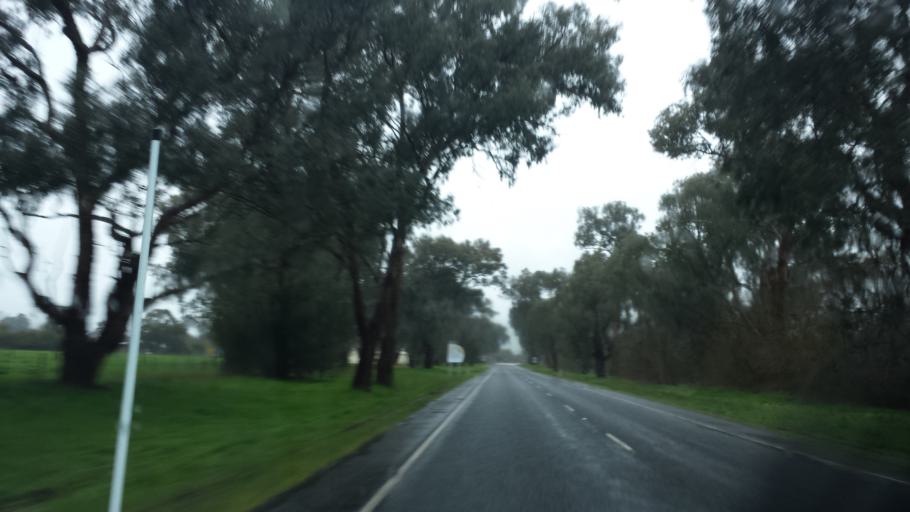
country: AU
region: Victoria
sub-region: Wangaratta
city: Wangaratta
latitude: -36.4323
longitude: 146.5355
